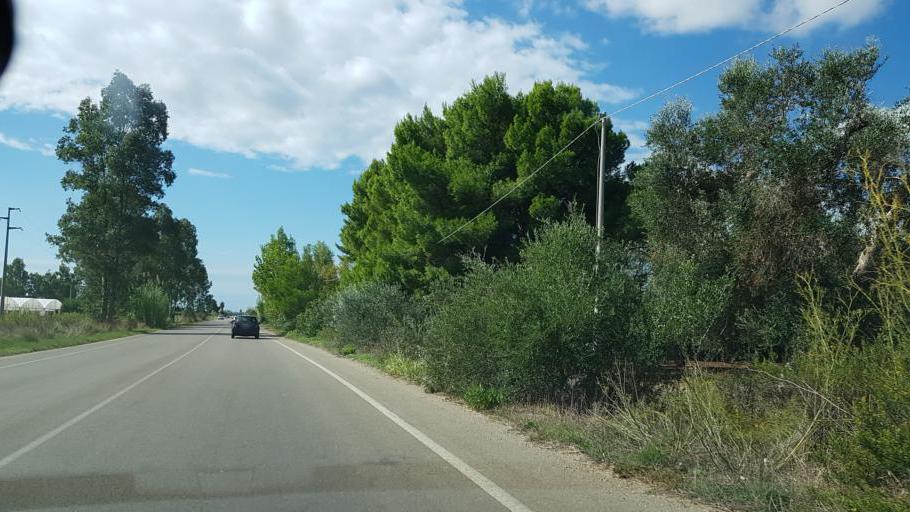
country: IT
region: Apulia
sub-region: Provincia di Lecce
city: Leverano
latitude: 40.3079
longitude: 18.0177
